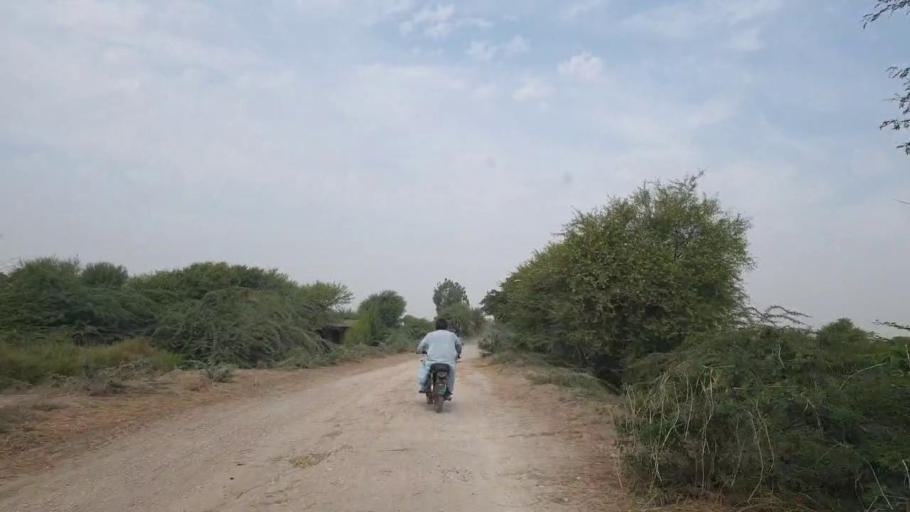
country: PK
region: Sindh
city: Rajo Khanani
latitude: 24.9460
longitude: 68.9803
